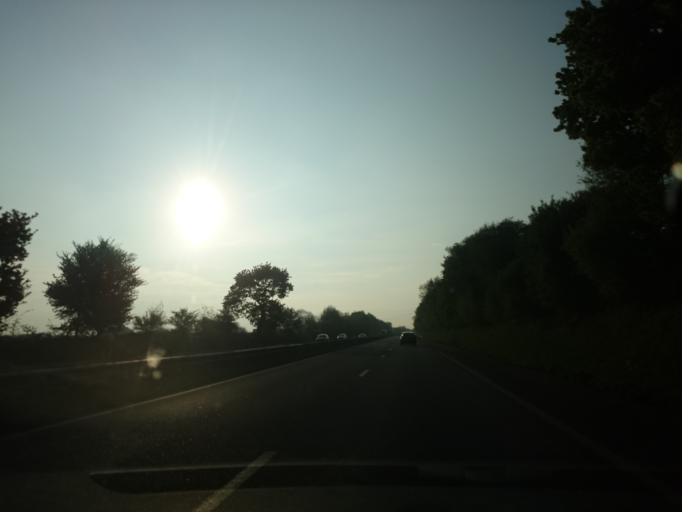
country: FR
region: Brittany
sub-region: Departement du Finistere
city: Melgven
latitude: 47.9088
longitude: -3.8597
